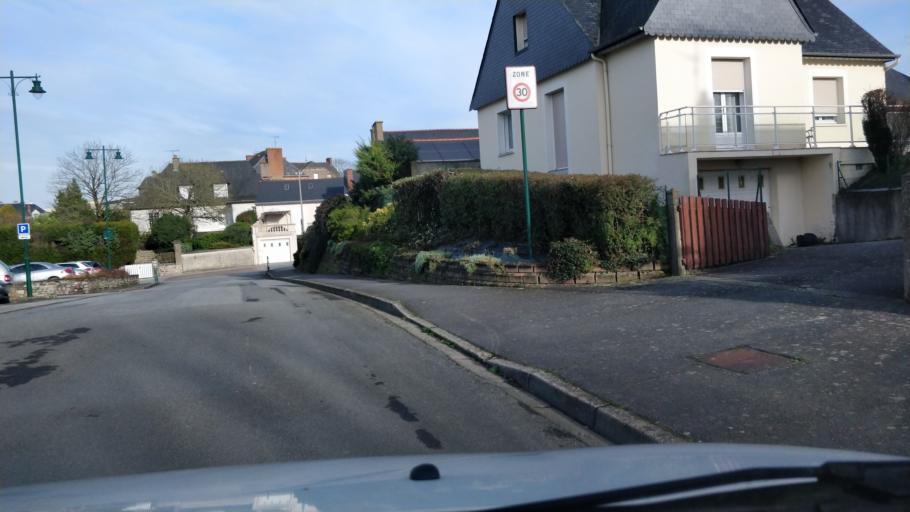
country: FR
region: Brittany
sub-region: Departement d'Ille-et-Vilaine
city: Argentre-du-Plessis
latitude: 48.0564
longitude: -1.1488
